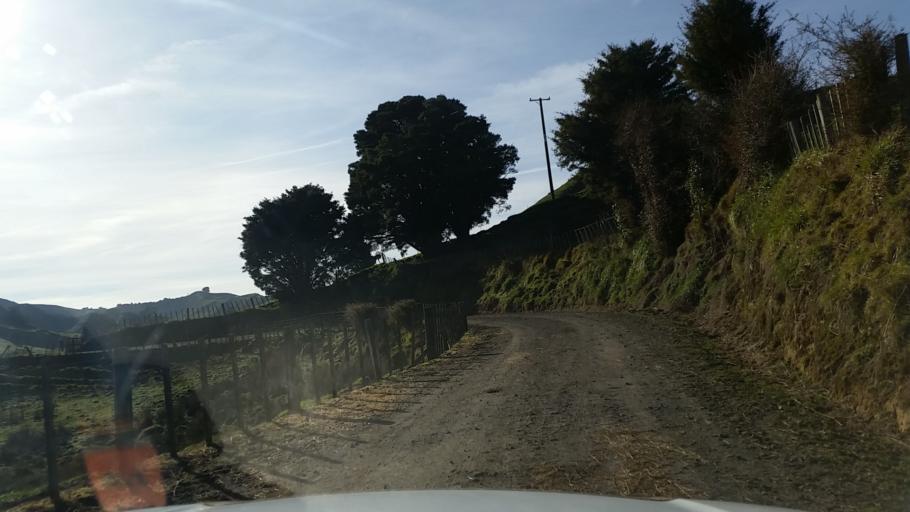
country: NZ
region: Taranaki
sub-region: South Taranaki District
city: Eltham
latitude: -39.3146
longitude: 174.5342
